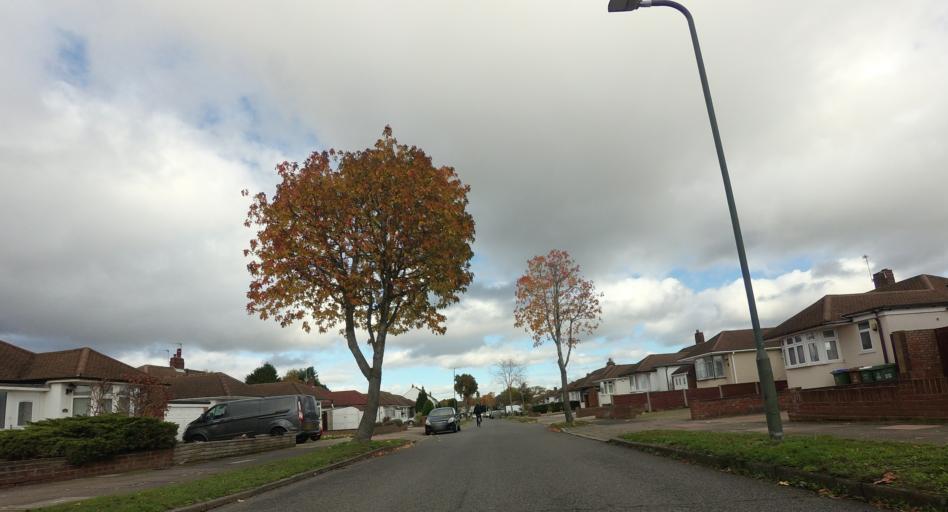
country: GB
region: England
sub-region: Greater London
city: Sidcup
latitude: 51.4306
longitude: 0.1180
